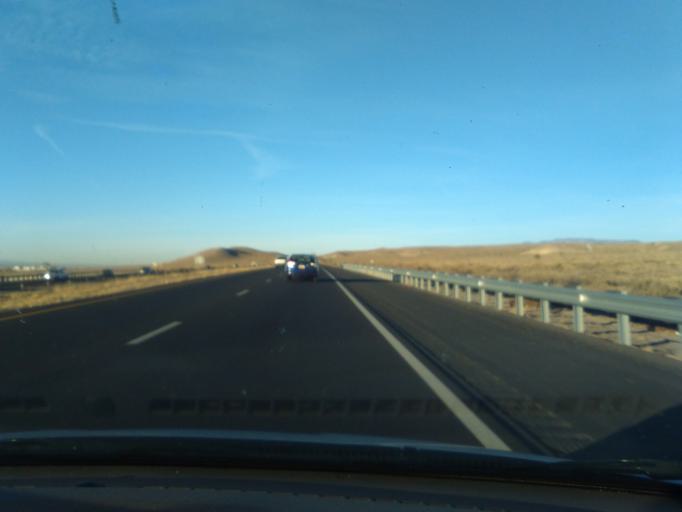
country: US
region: New Mexico
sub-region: Bernalillo County
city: South Valley
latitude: 34.9730
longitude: -106.6541
